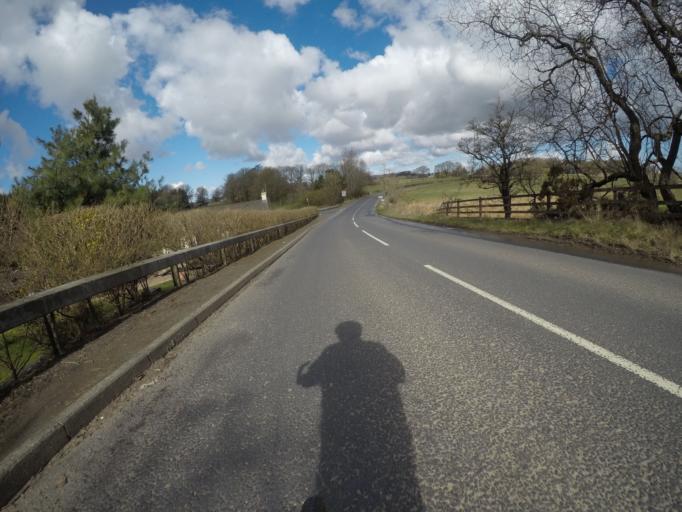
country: GB
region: Scotland
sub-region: North Ayrshire
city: Beith
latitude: 55.7394
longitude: -4.6243
